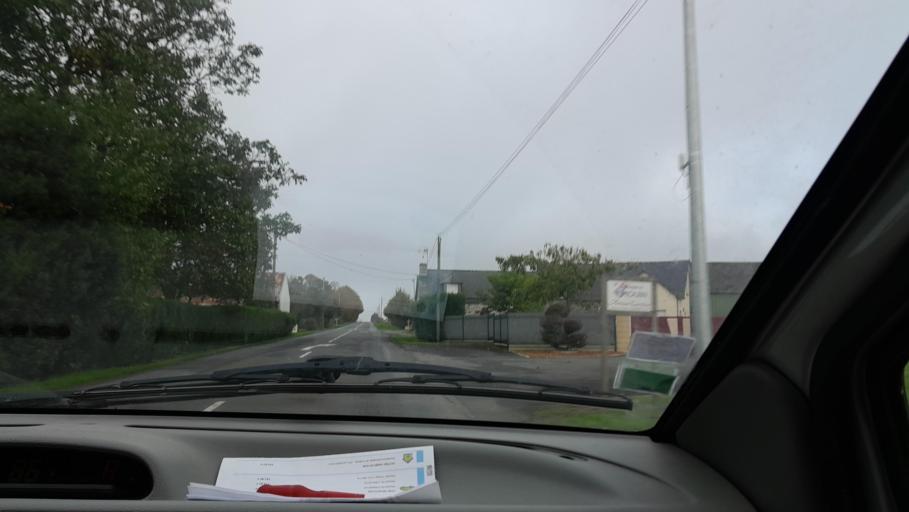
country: FR
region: Brittany
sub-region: Departement d'Ille-et-Vilaine
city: Luitre
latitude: 48.2418
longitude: -1.1145
